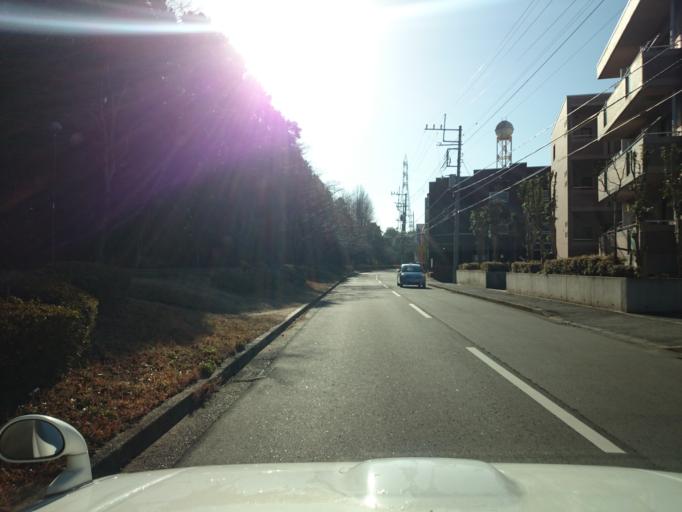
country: JP
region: Ibaraki
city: Naka
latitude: 36.1008
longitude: 140.1008
